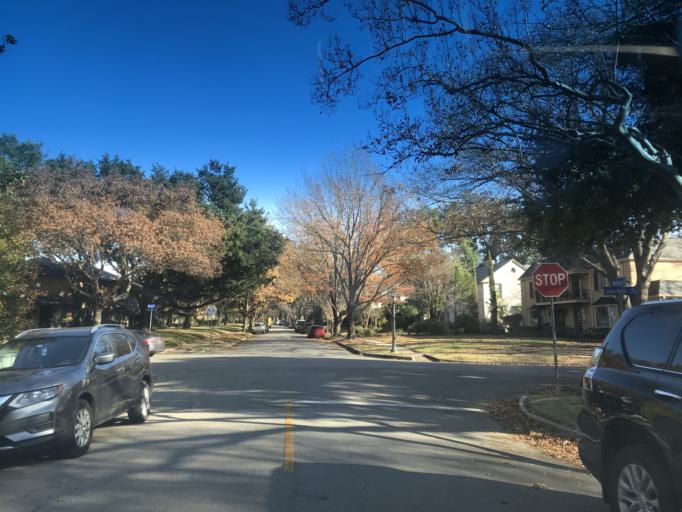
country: US
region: Texas
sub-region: Dallas County
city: Highland Park
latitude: 32.8238
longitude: -96.8128
